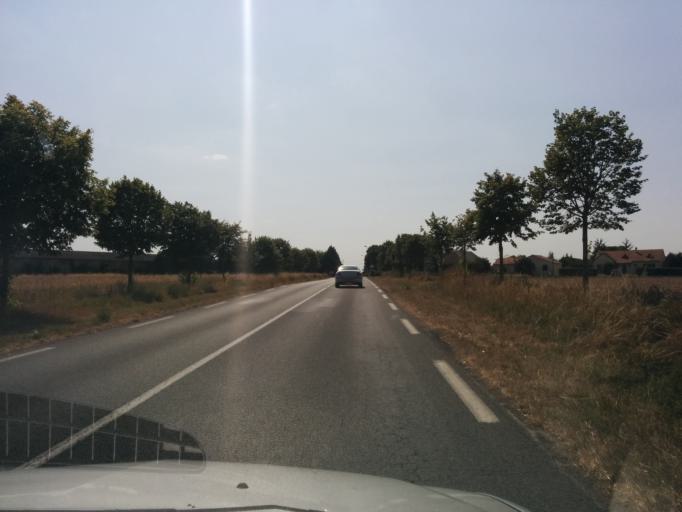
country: FR
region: Poitou-Charentes
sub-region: Departement de la Vienne
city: Neuville-de-Poitou
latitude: 46.6877
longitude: 0.2787
